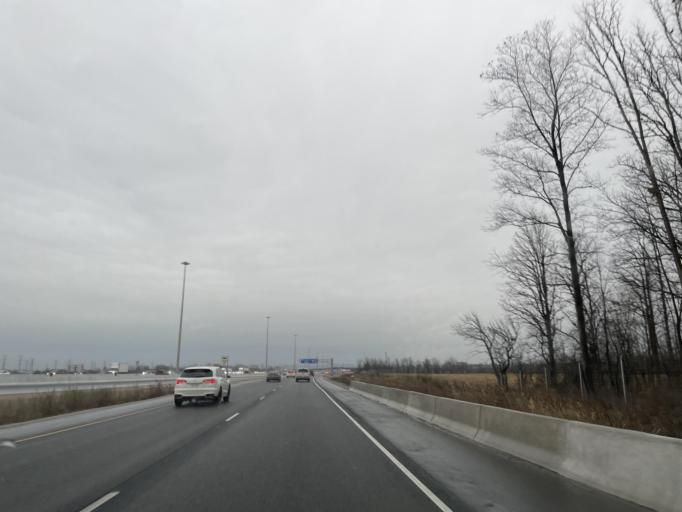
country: CA
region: Ontario
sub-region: Halton
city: Milton
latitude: 43.5802
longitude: -79.8202
